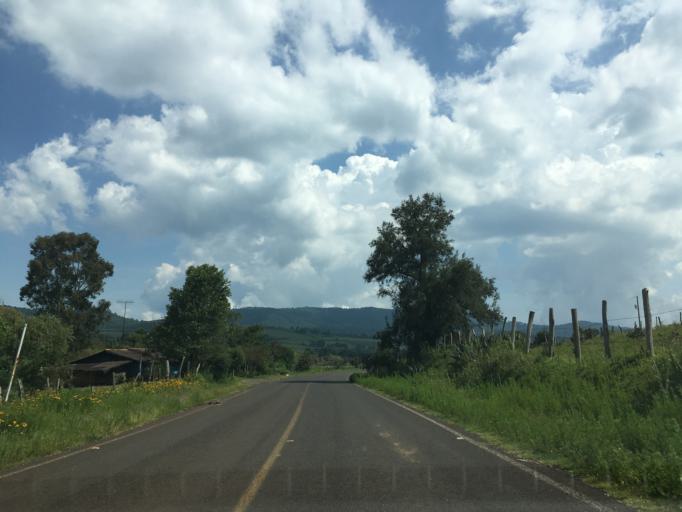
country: MX
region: Michoacan
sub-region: Morelia
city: Montana Monarca (Punta Altozano)
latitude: 19.6042
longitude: -101.1942
